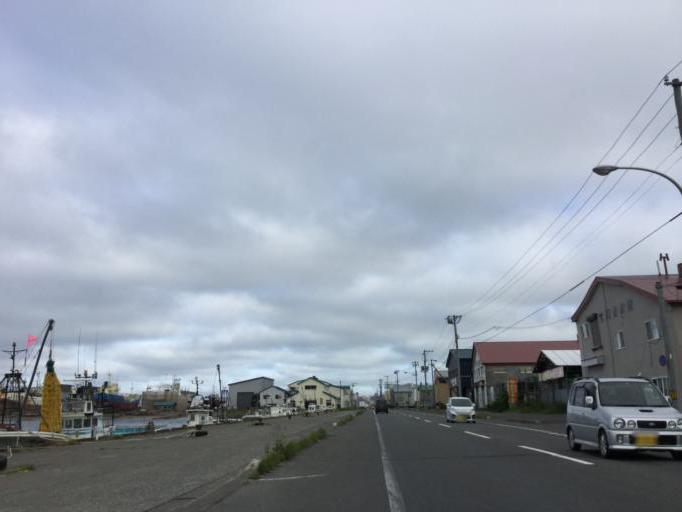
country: JP
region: Hokkaido
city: Wakkanai
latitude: 45.4039
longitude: 141.6791
